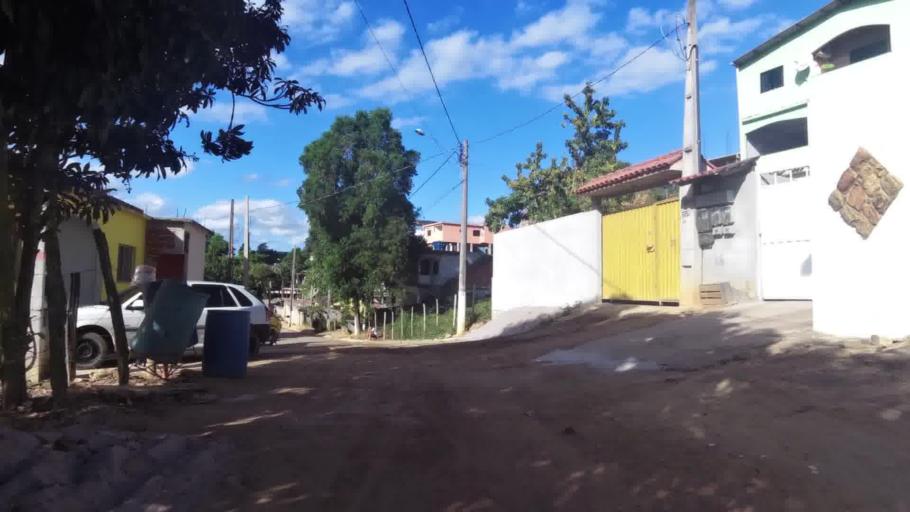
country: BR
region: Espirito Santo
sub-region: Marataizes
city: Marataizes
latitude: -21.1020
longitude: -41.0497
